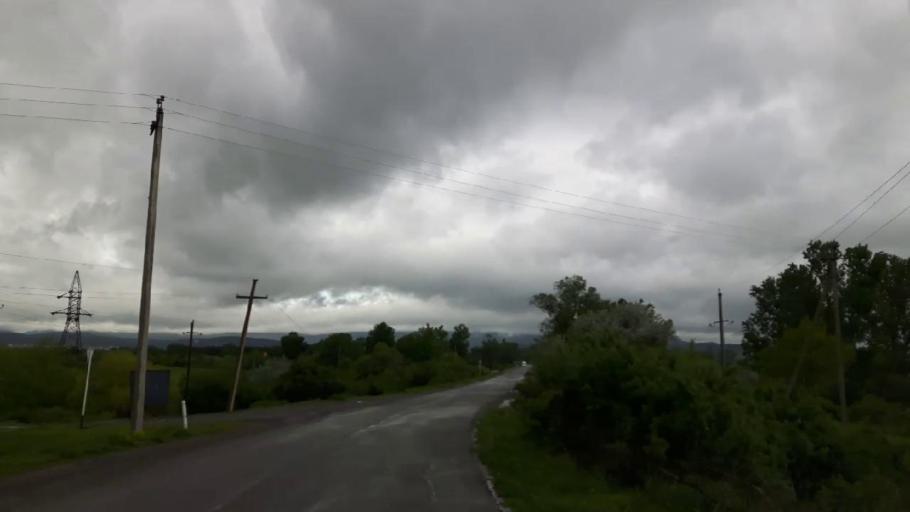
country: GE
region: Shida Kartli
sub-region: Khashuris Raioni
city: Khashuri
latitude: 41.9897
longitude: 43.6600
